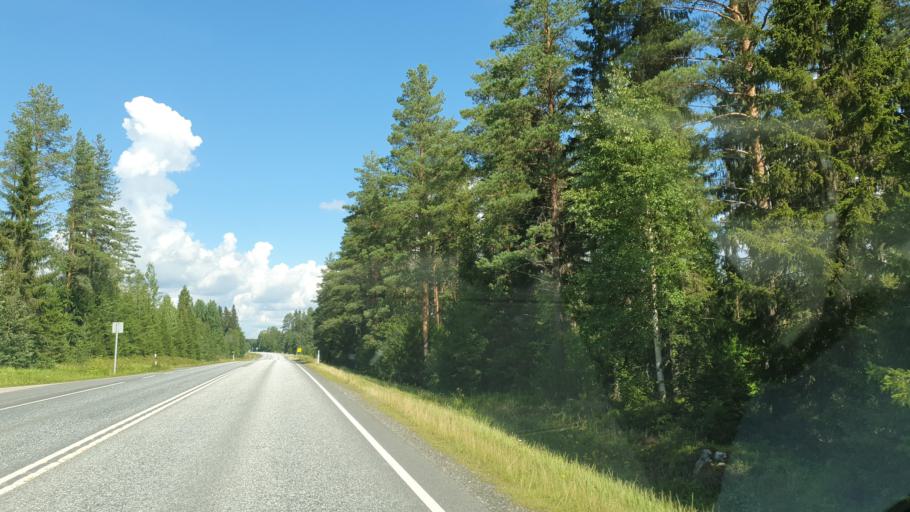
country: FI
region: Northern Savo
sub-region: Ylae-Savo
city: Sonkajaervi
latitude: 63.7935
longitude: 27.4186
